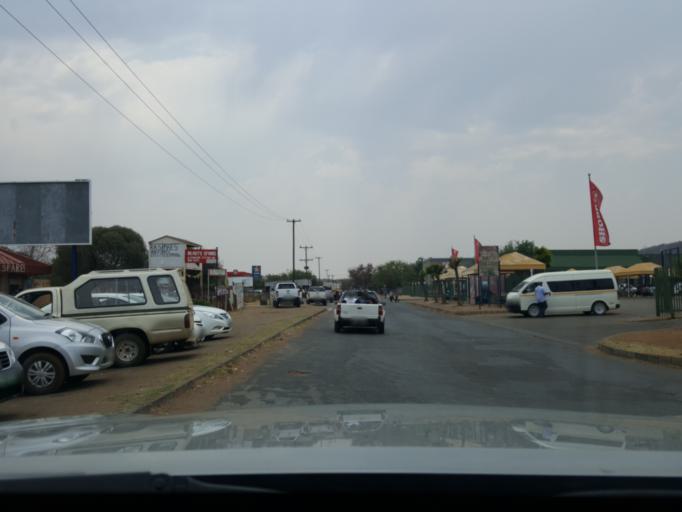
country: ZA
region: North-West
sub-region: Ngaka Modiri Molema District Municipality
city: Zeerust
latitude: -25.4945
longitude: 25.9841
